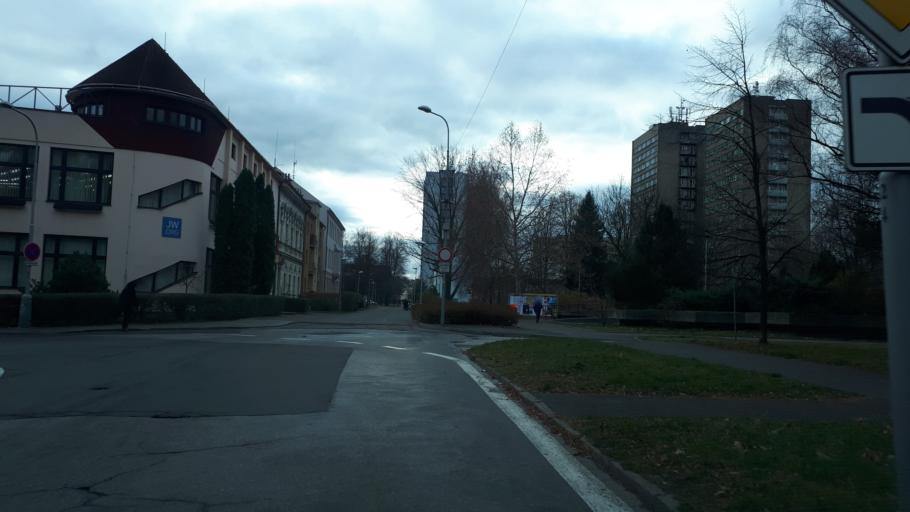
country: CZ
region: Moravskoslezsky
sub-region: Okres Frydek-Mistek
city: Frydek-Mistek
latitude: 49.6805
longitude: 18.3405
